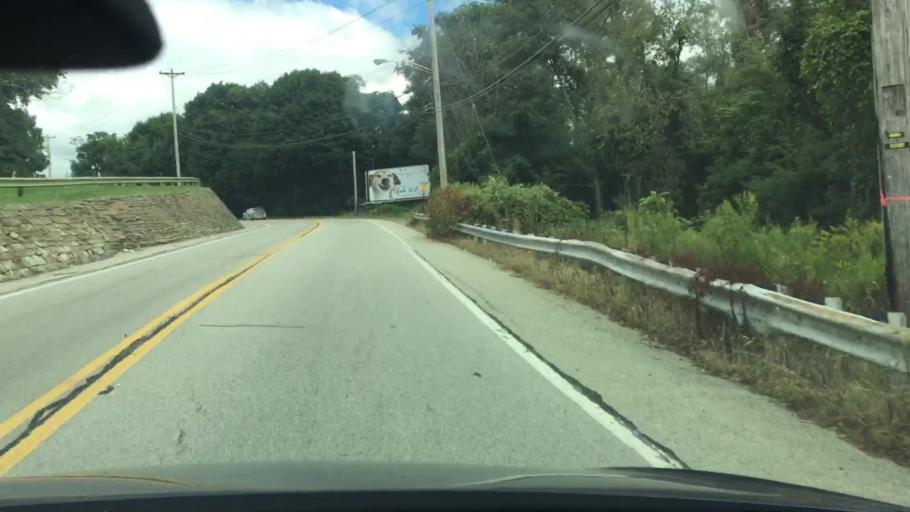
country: US
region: Pennsylvania
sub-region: Allegheny County
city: Penn Hills
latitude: 40.4754
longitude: -79.8220
